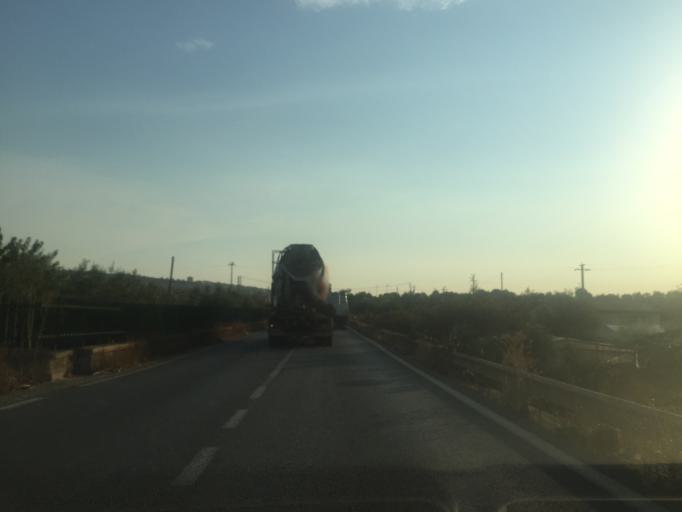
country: IT
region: Sicily
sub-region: Ragusa
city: Ispica
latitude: 36.7610
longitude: 14.8960
